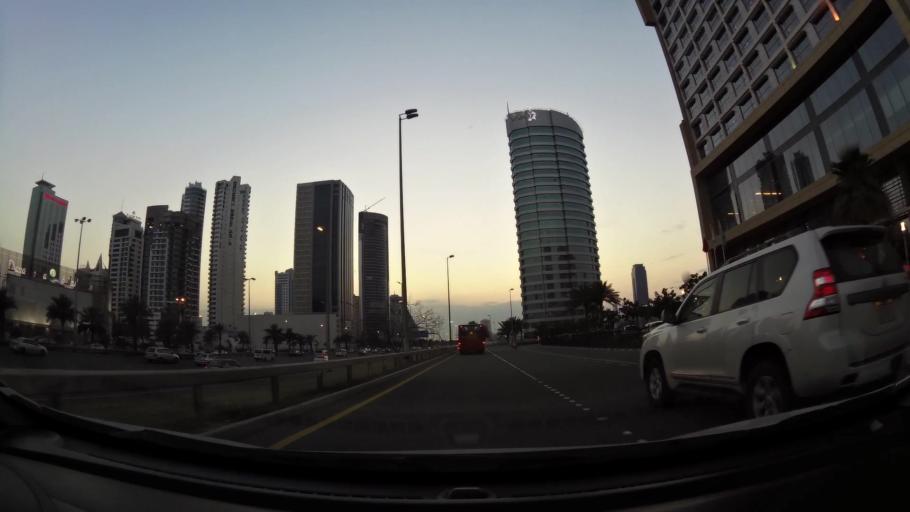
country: BH
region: Manama
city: Jidd Hafs
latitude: 26.2315
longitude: 50.5530
